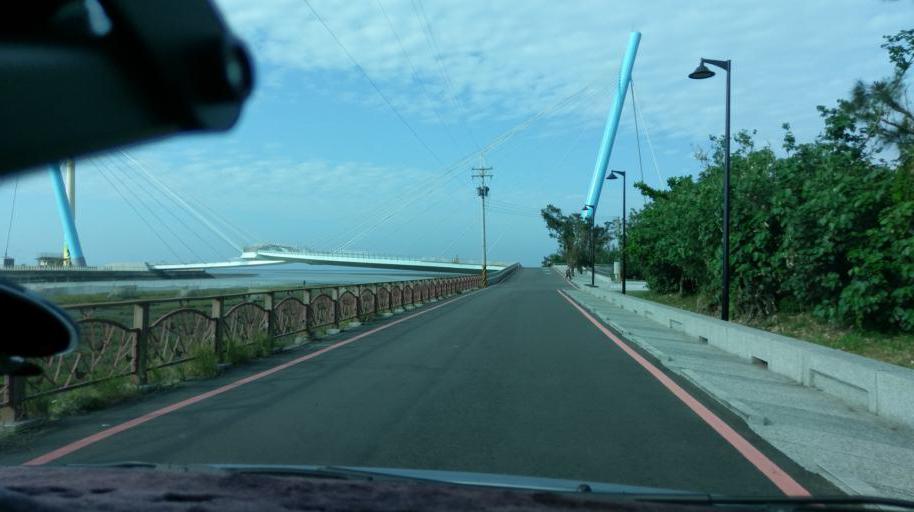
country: TW
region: Taiwan
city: Fengyuan
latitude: 24.3020
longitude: 120.5463
